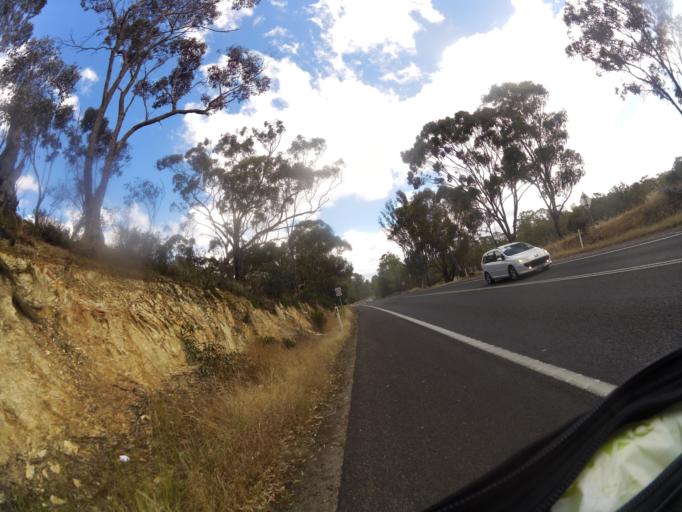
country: AU
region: Victoria
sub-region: Mount Alexander
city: Castlemaine
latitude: -37.0387
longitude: 144.2269
